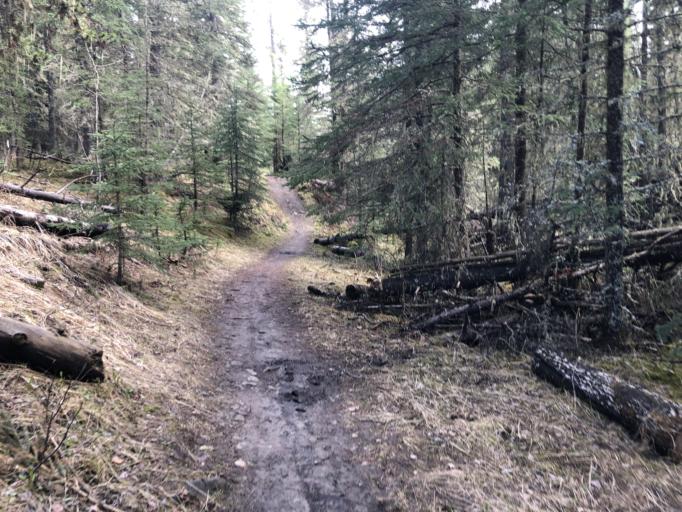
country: CA
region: Alberta
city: Cochrane
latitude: 51.0368
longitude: -114.7314
